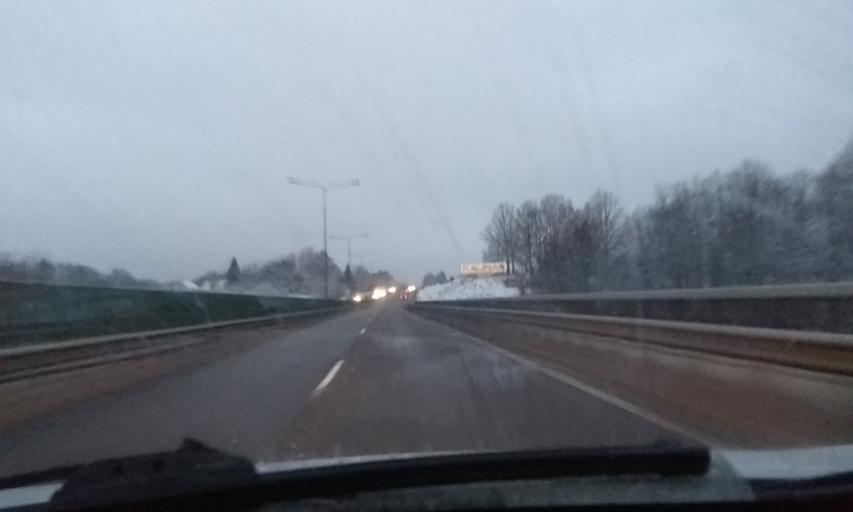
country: LT
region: Kauno apskritis
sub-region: Kauno rajonas
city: Karmelava
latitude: 54.9126
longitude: 24.1008
